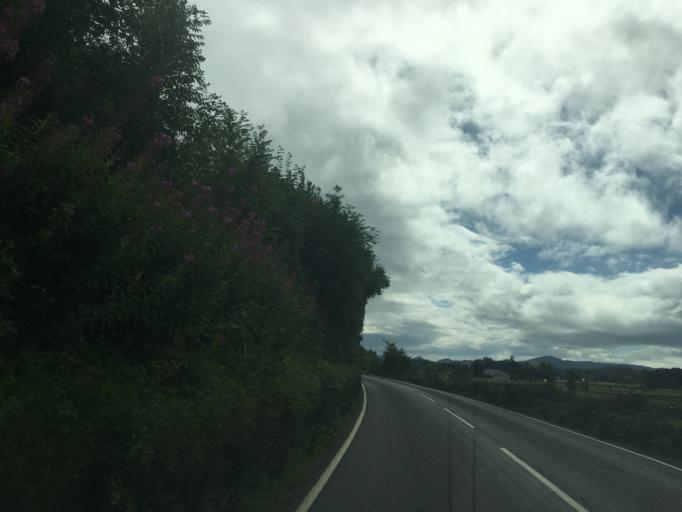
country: GB
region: Scotland
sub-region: Argyll and Bute
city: Lochgilphead
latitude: 56.1304
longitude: -5.4854
